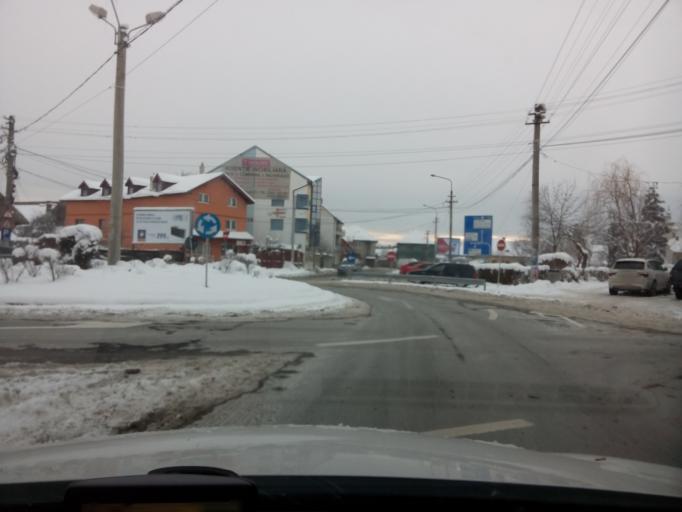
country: RO
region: Sibiu
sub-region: Municipiul Sibiu
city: Sibiu
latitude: 45.8012
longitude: 24.1435
